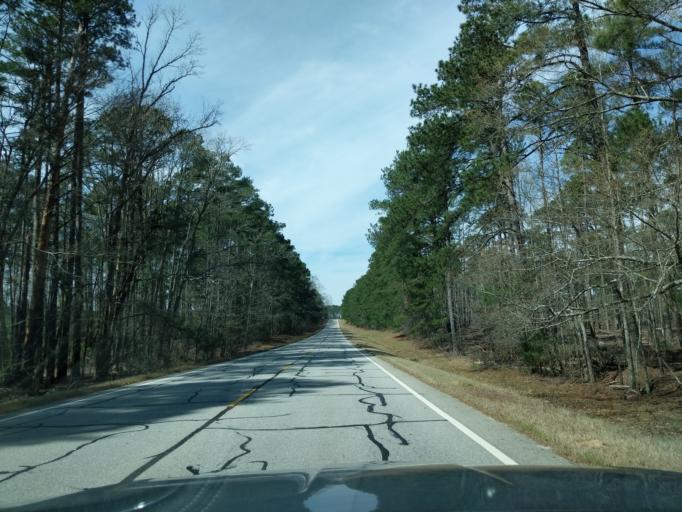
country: US
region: Georgia
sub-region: Columbia County
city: Appling
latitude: 33.6523
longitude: -82.2287
